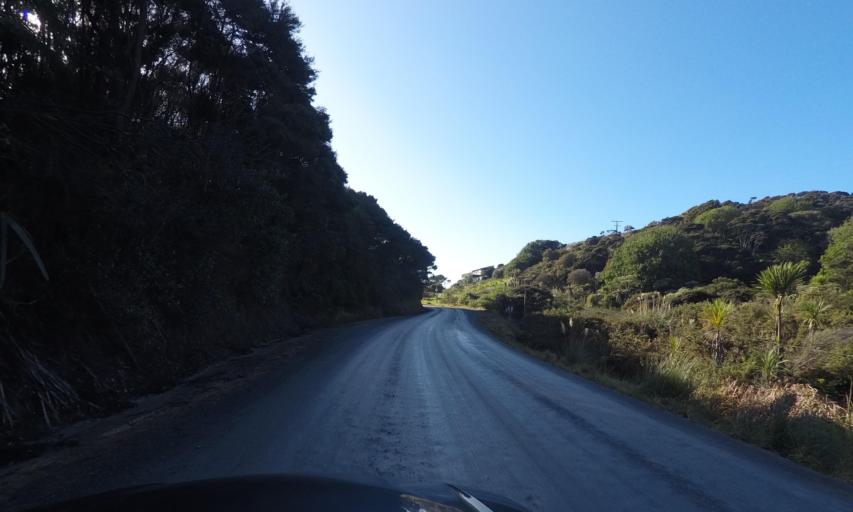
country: NZ
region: Auckland
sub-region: Auckland
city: Wellsford
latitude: -36.1612
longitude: 174.6413
